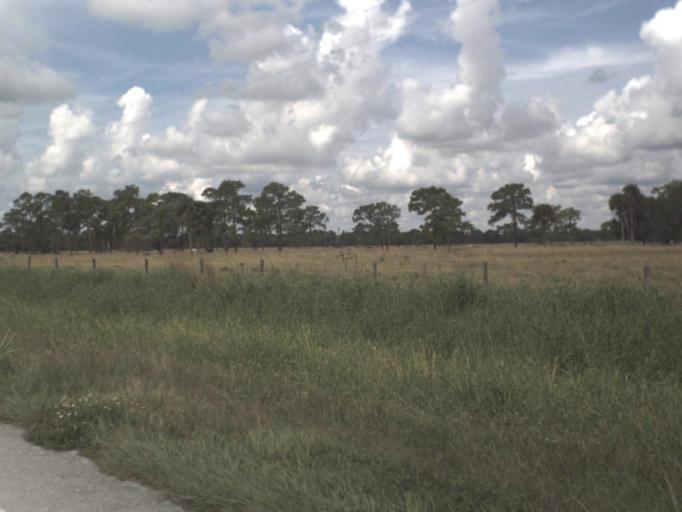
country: US
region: Florida
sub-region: Okeechobee County
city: Okeechobee
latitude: 27.2436
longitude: -80.8889
